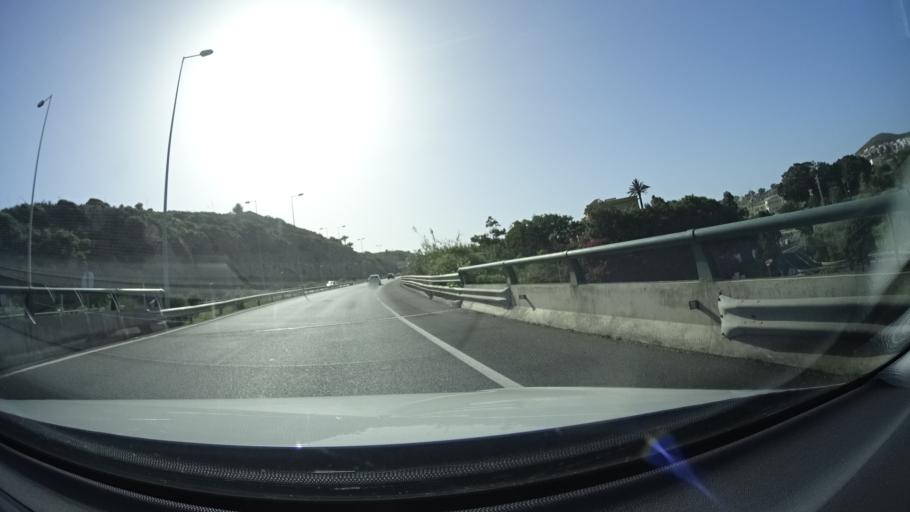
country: ES
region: Canary Islands
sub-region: Provincia de Las Palmas
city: Santa Brigida
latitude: 28.0505
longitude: -15.4475
